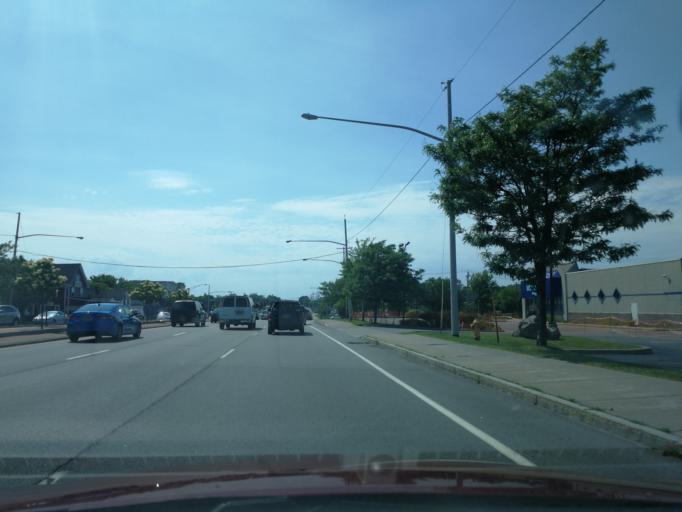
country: US
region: New York
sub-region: Monroe County
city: Greece
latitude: 43.2049
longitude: -77.6643
